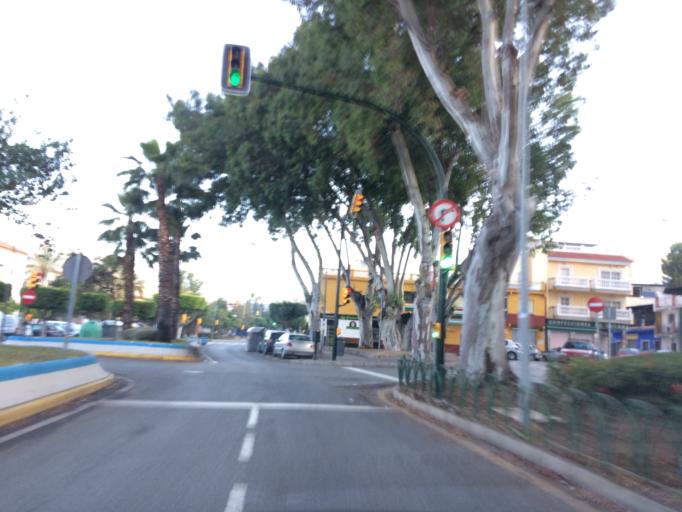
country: ES
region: Andalusia
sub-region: Provincia de Malaga
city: Malaga
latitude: 36.7494
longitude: -4.4218
